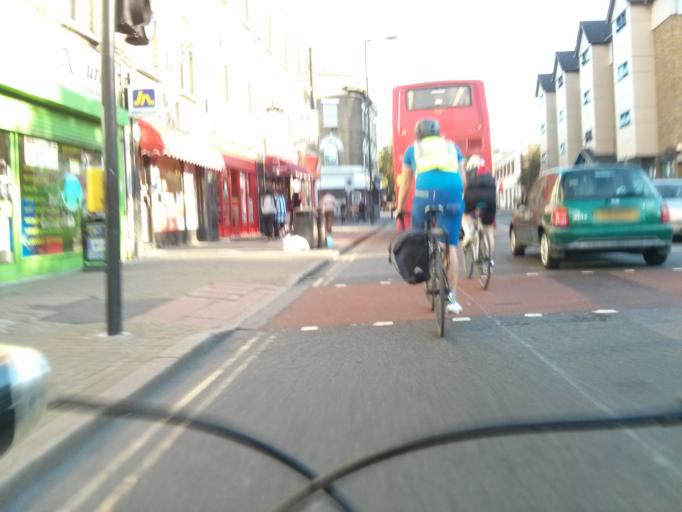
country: GB
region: England
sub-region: Greater London
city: Camberwell
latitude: 51.4719
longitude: -0.0930
